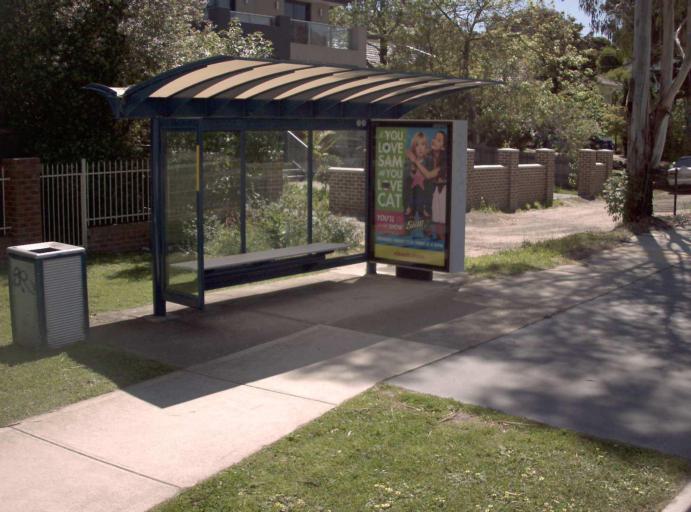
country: AU
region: Victoria
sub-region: Whitehorse
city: Blackburn North
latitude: -37.7991
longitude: 145.1600
